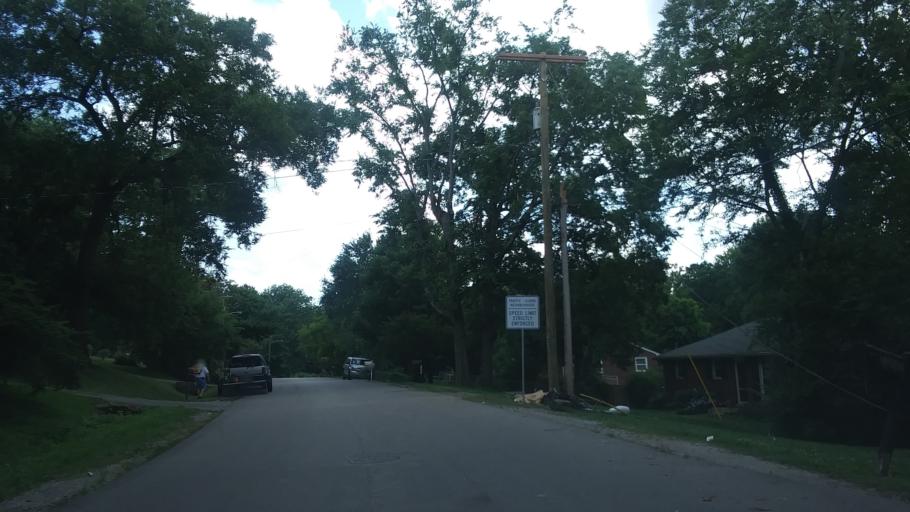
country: US
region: Tennessee
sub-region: Davidson County
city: Oak Hill
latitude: 36.0670
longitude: -86.7004
